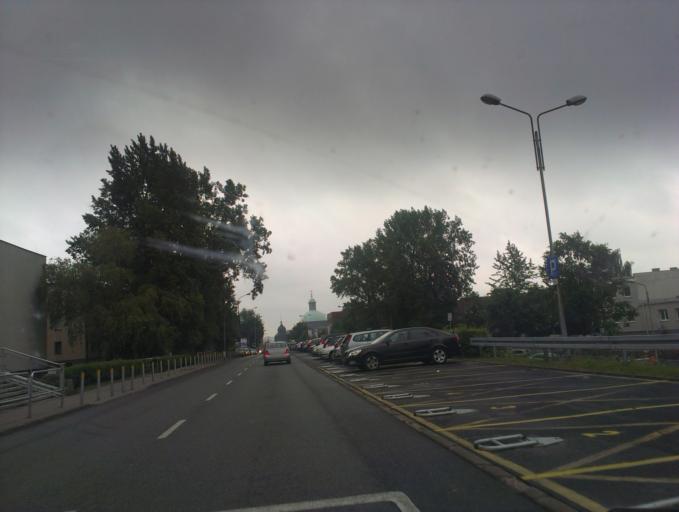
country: PL
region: Silesian Voivodeship
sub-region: Katowice
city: Katowice
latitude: 50.2471
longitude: 19.0166
